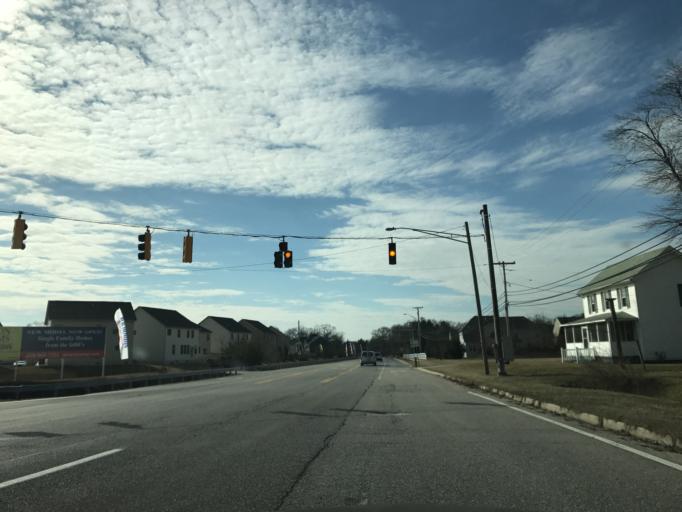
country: US
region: Maryland
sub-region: Anne Arundel County
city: South Gate
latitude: 39.1223
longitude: -76.6446
